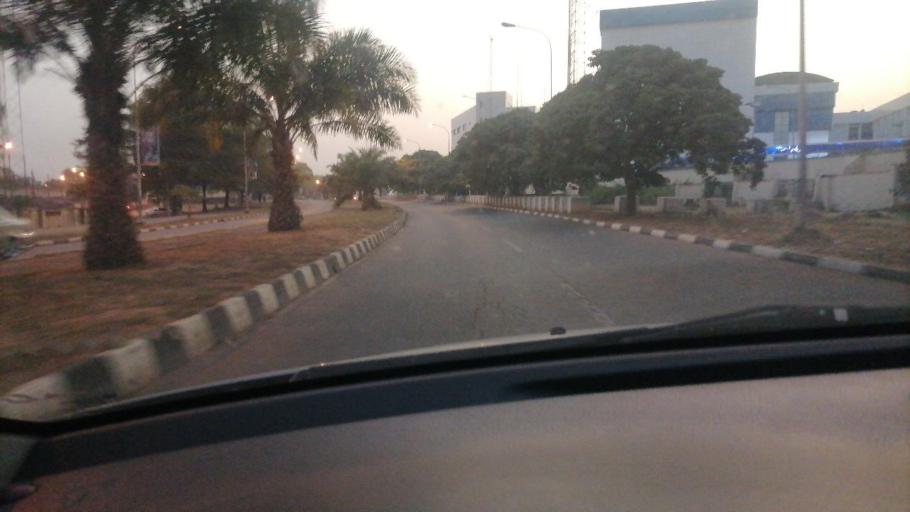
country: NG
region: Abuja Federal Capital Territory
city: Abuja
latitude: 9.0395
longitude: 7.4910
